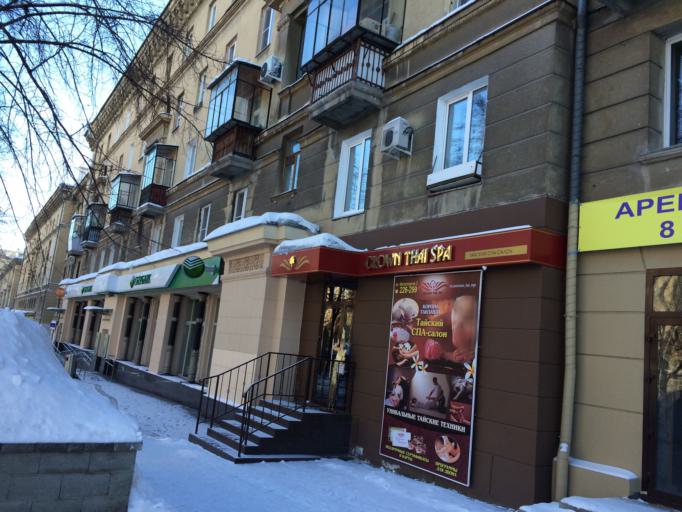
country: RU
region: Chelyabinsk
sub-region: Gorod Magnitogorsk
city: Magnitogorsk
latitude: 53.4220
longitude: 58.9968
